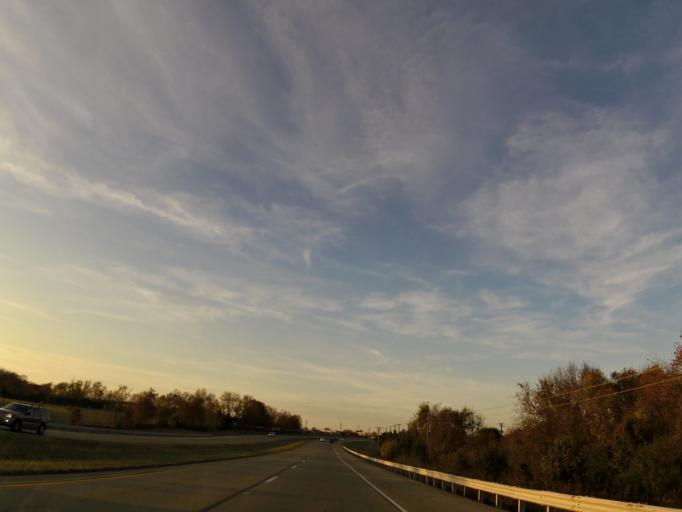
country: US
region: Kentucky
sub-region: Jessamine County
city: Nicholasville
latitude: 37.8665
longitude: -84.5957
